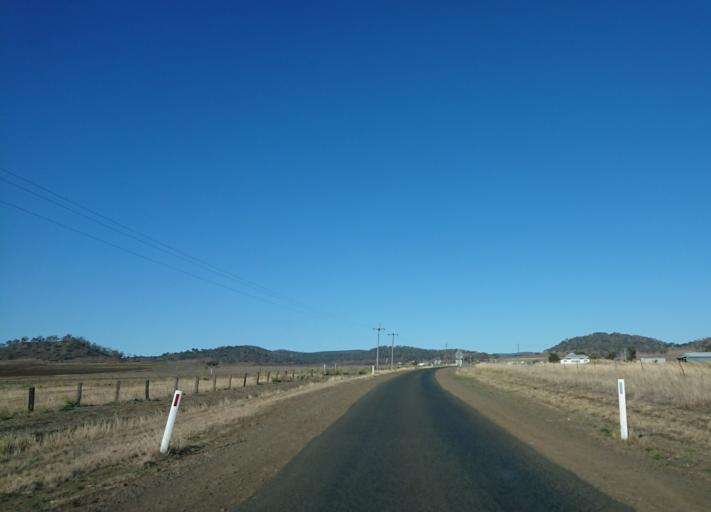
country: AU
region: Queensland
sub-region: Toowoomba
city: Top Camp
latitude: -27.8189
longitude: 152.0022
